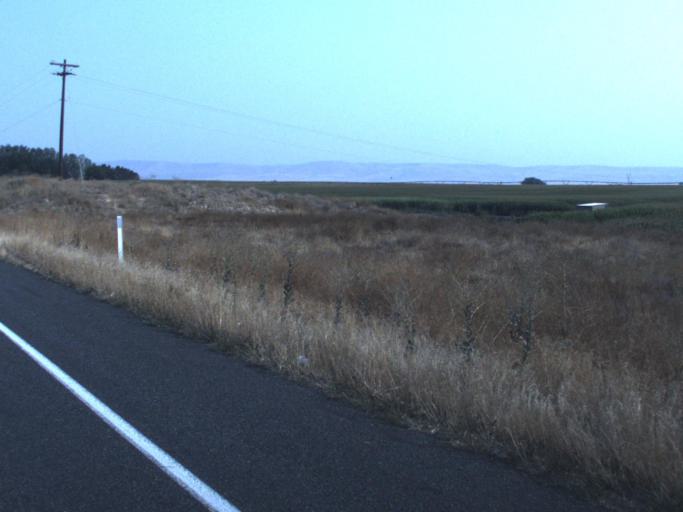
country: US
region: Washington
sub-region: Yakima County
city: Mabton
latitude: 46.2261
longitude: -120.0584
